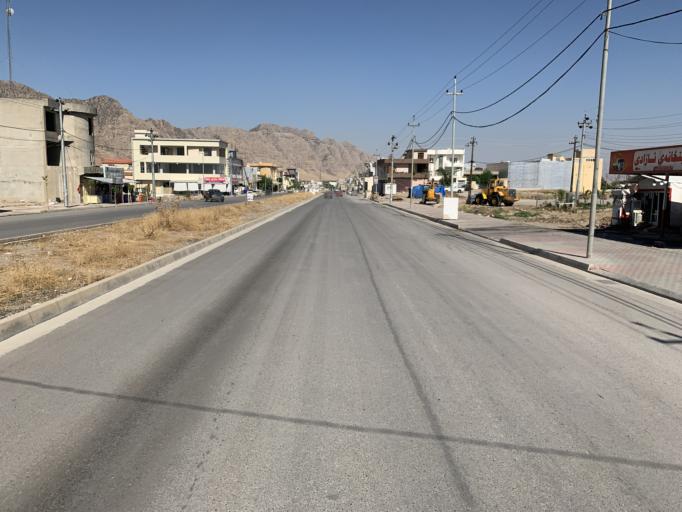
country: IQ
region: As Sulaymaniyah
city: Raniye
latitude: 36.2588
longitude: 44.8661
